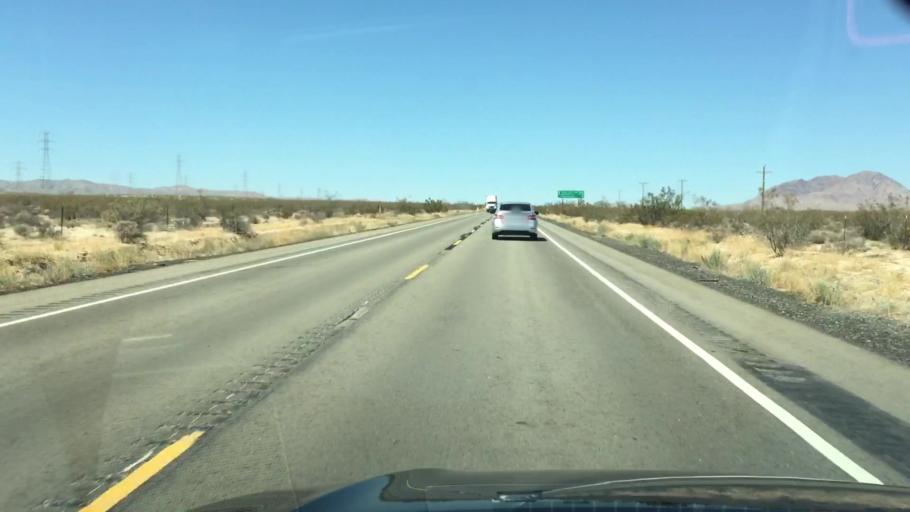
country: US
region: California
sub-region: Kern County
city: Boron
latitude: 35.2503
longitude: -117.6114
